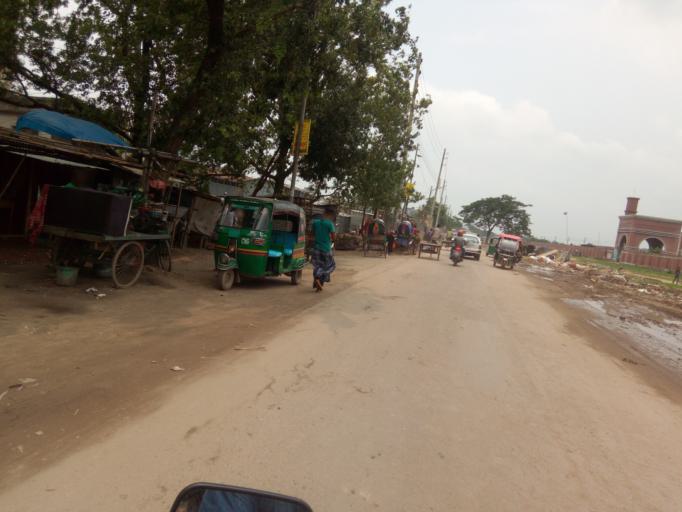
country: BD
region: Dhaka
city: Azimpur
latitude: 23.7499
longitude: 90.3582
